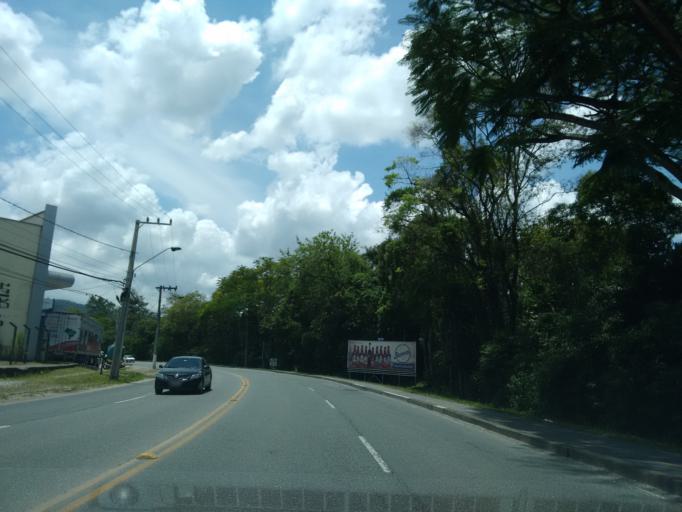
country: BR
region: Santa Catarina
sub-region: Blumenau
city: Blumenau
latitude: -26.9086
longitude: -49.0460
